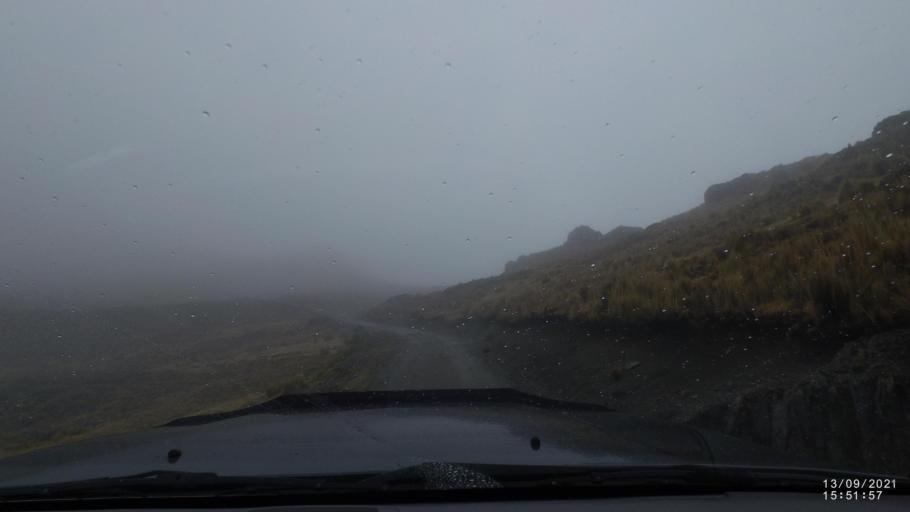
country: BO
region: Cochabamba
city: Colomi
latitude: -17.3049
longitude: -65.7130
